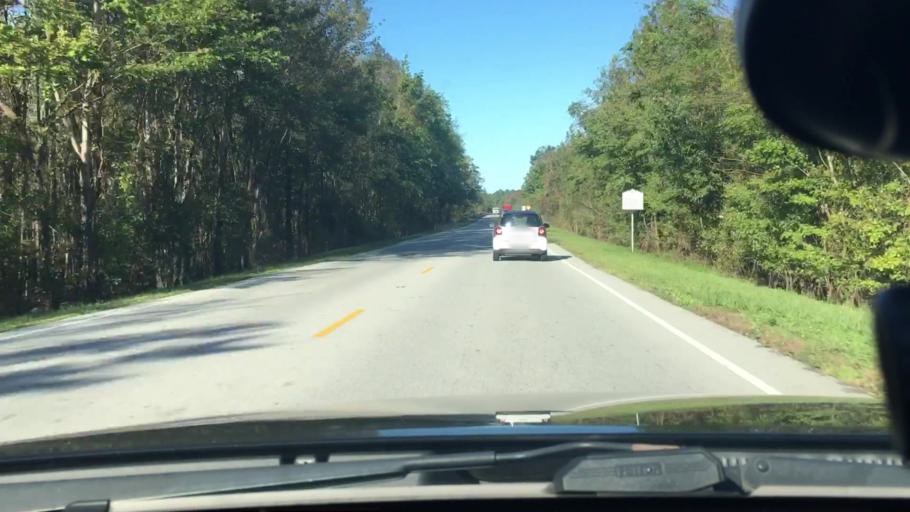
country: US
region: North Carolina
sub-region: Craven County
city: Vanceboro
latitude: 35.2080
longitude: -77.1246
